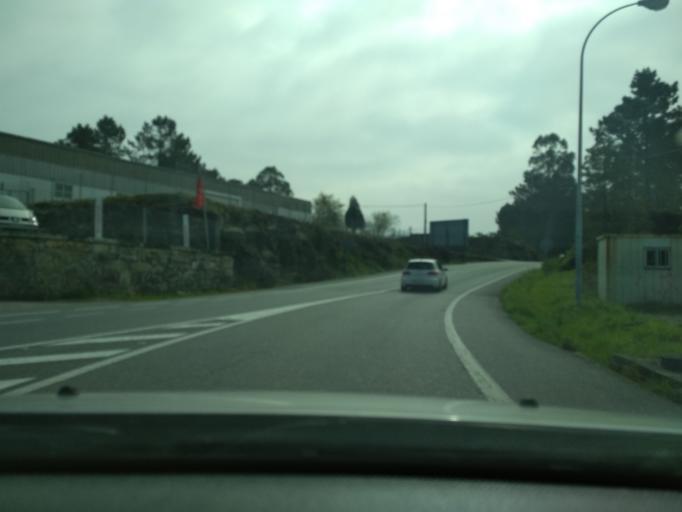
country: ES
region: Galicia
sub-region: Provincia de Pontevedra
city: Catoira
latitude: 42.6717
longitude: -8.7095
